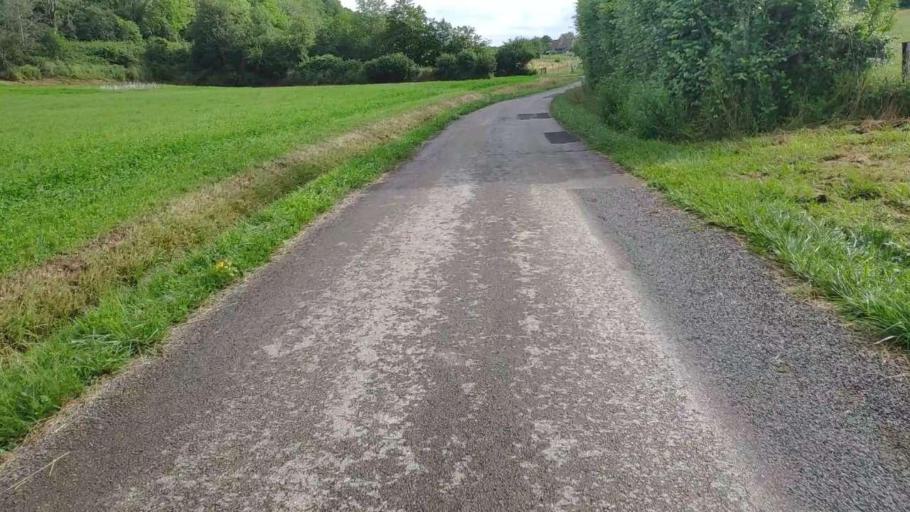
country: FR
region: Franche-Comte
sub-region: Departement du Jura
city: Poligny
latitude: 46.8274
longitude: 5.5803
